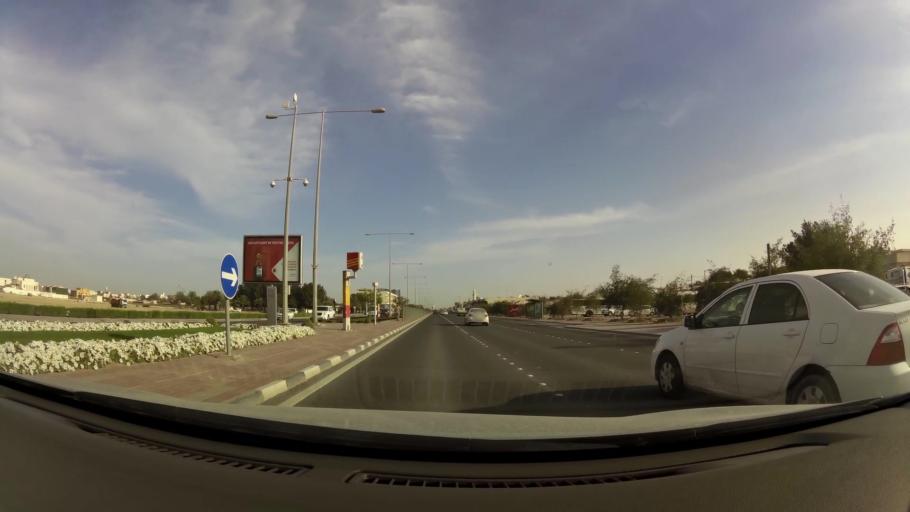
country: QA
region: Al Wakrah
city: Al Wakrah
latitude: 25.1848
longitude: 51.6006
